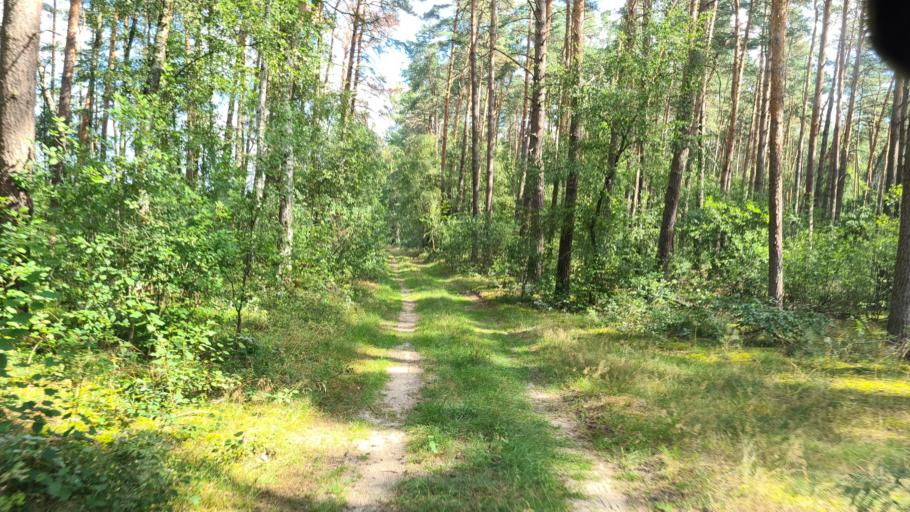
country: DE
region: Brandenburg
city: Sonnewalde
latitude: 51.7403
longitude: 13.6946
